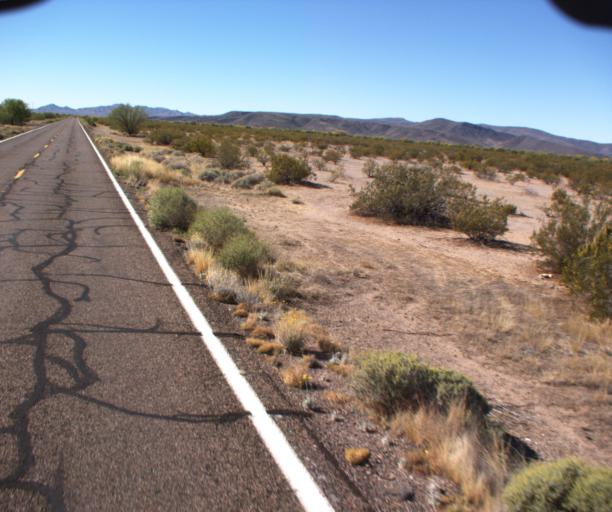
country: US
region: Arizona
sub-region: Pima County
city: Ajo
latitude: 32.5254
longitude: -112.8804
